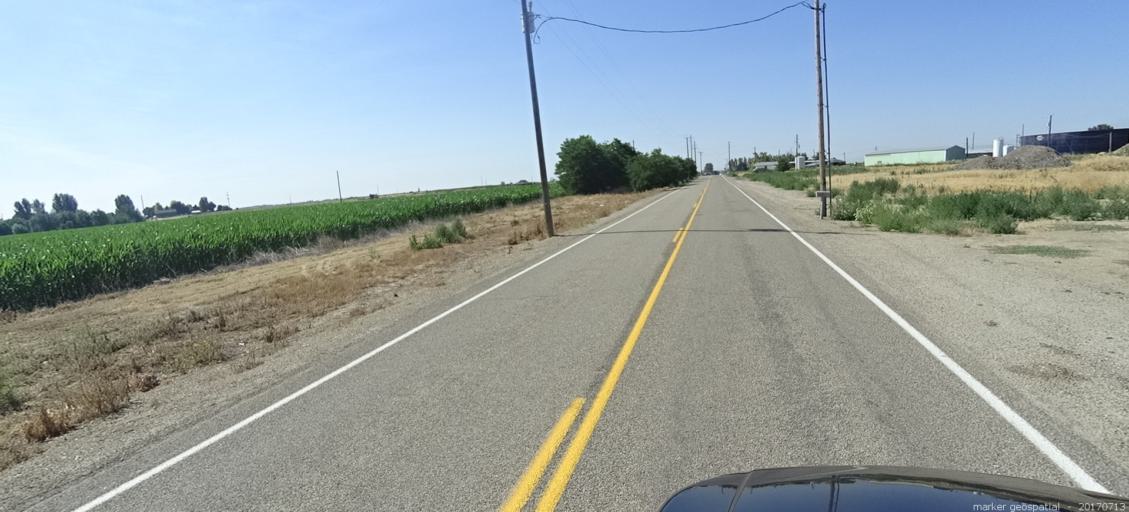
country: US
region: Idaho
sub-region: Ada County
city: Kuna
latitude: 43.5361
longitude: -116.3743
